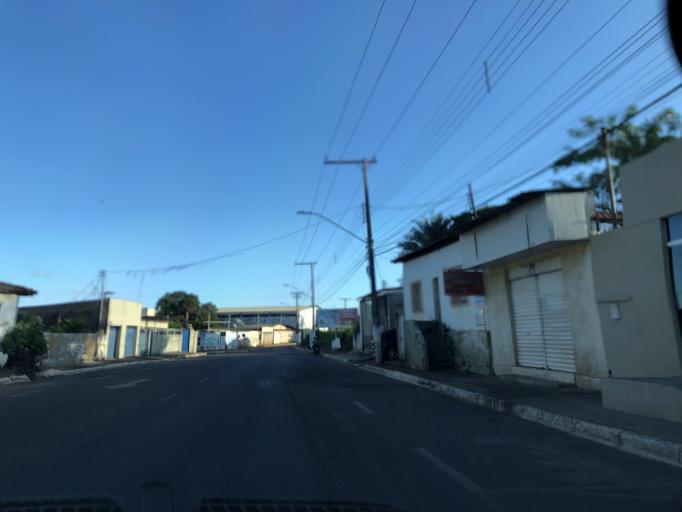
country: BR
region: Goias
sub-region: Luziania
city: Luziania
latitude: -16.2579
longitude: -47.9515
